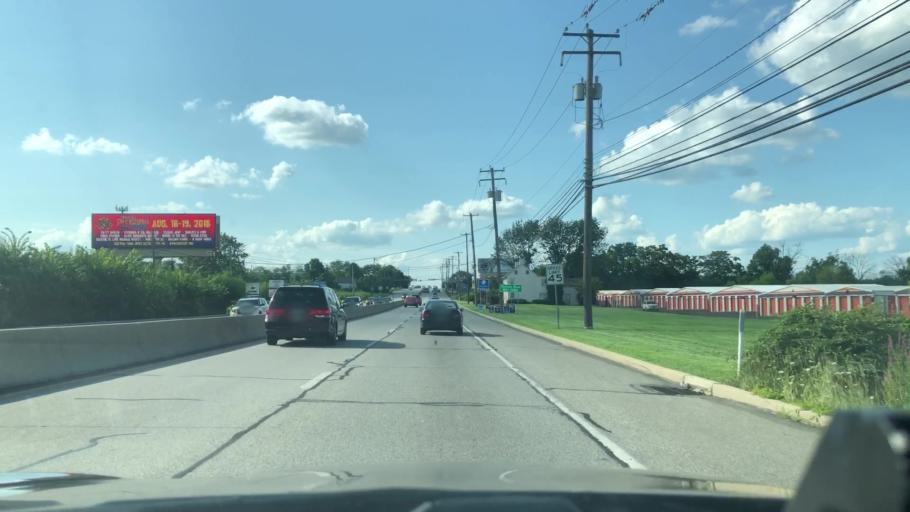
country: US
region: Pennsylvania
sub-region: Montgomery County
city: Spring House
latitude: 40.2136
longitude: -75.2266
